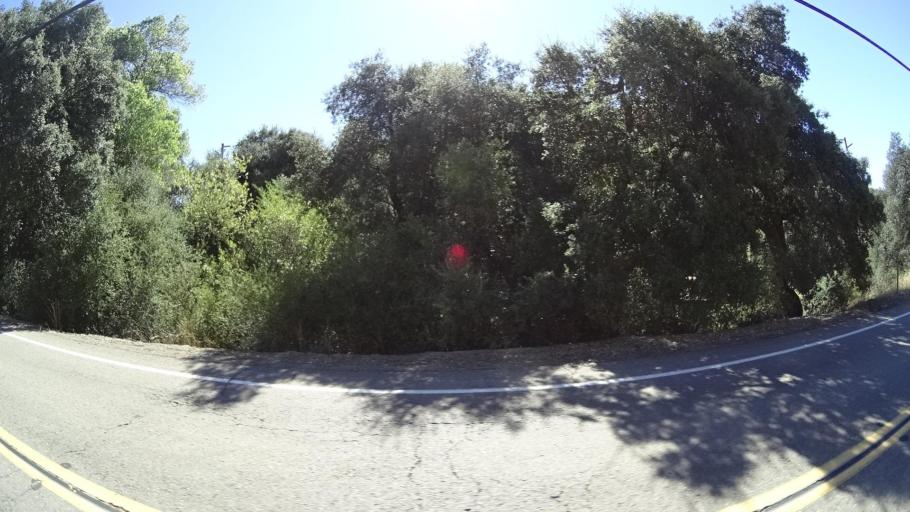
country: US
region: California
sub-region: San Diego County
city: Descanso
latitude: 32.8132
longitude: -116.6319
